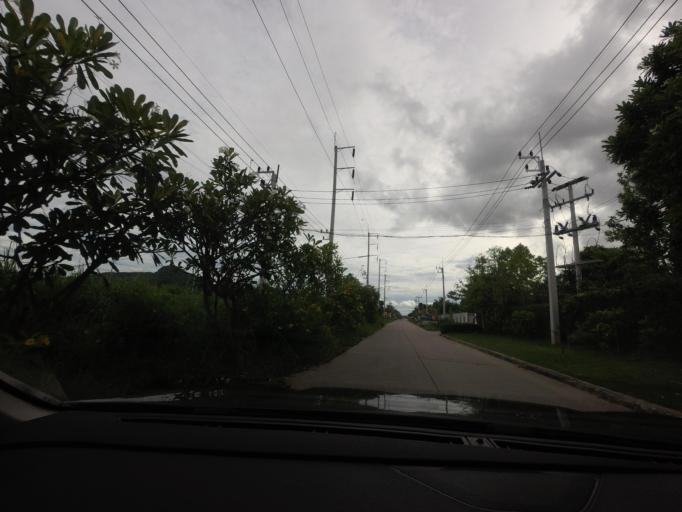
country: TH
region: Prachuap Khiri Khan
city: Hua Hin
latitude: 12.5385
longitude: 99.9473
